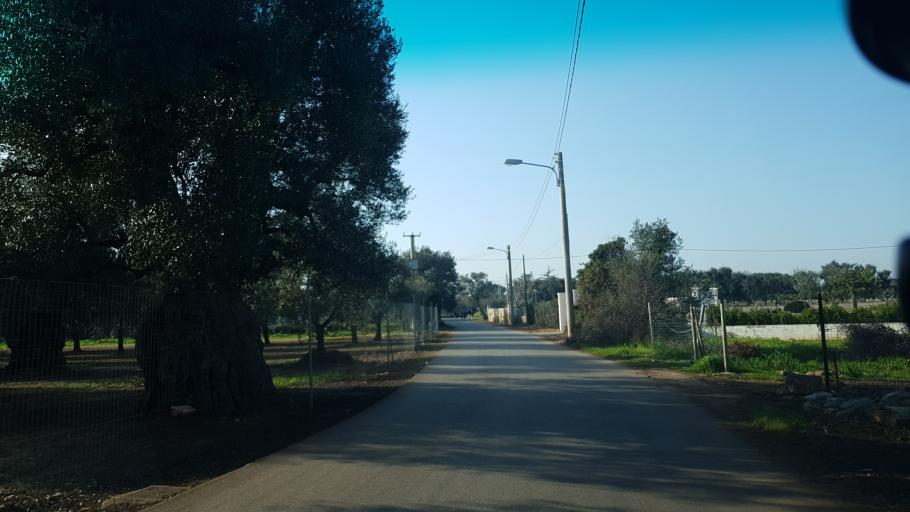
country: IT
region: Apulia
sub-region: Provincia di Brindisi
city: San Vito dei Normanni
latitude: 40.6646
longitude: 17.6930
